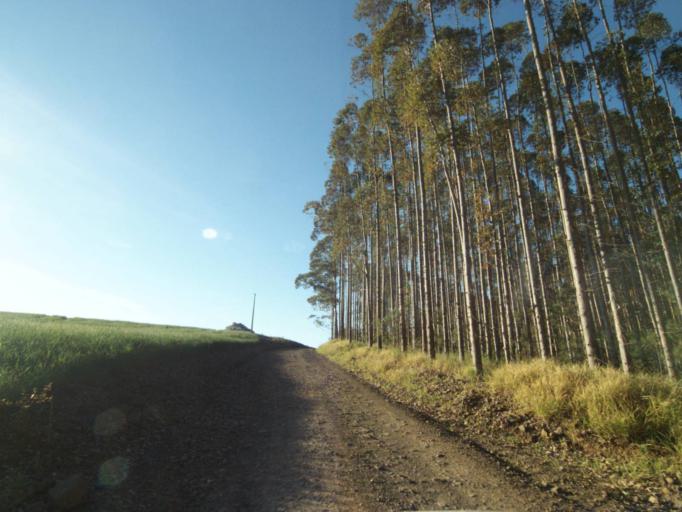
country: BR
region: Parana
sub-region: Telemaco Borba
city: Telemaco Borba
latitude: -24.4897
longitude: -50.5943
